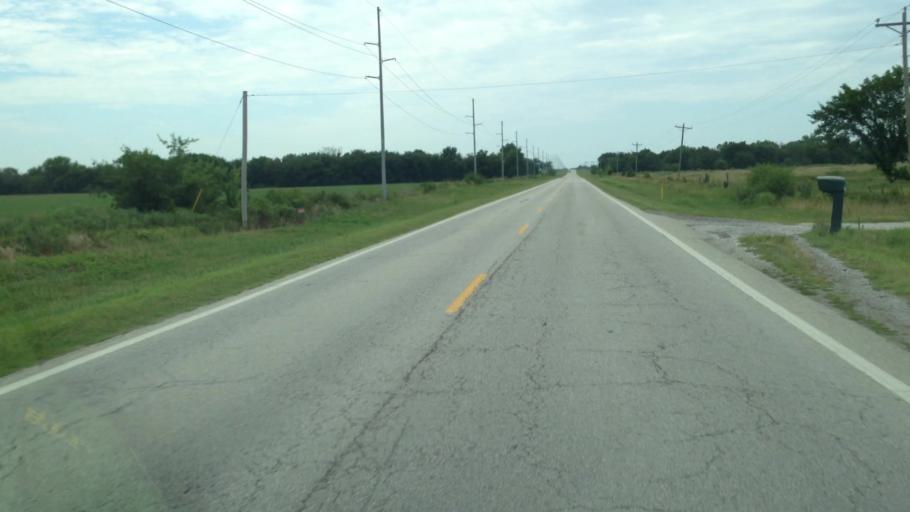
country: US
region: Kansas
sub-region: Labette County
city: Chetopa
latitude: 36.9054
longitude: -95.0896
